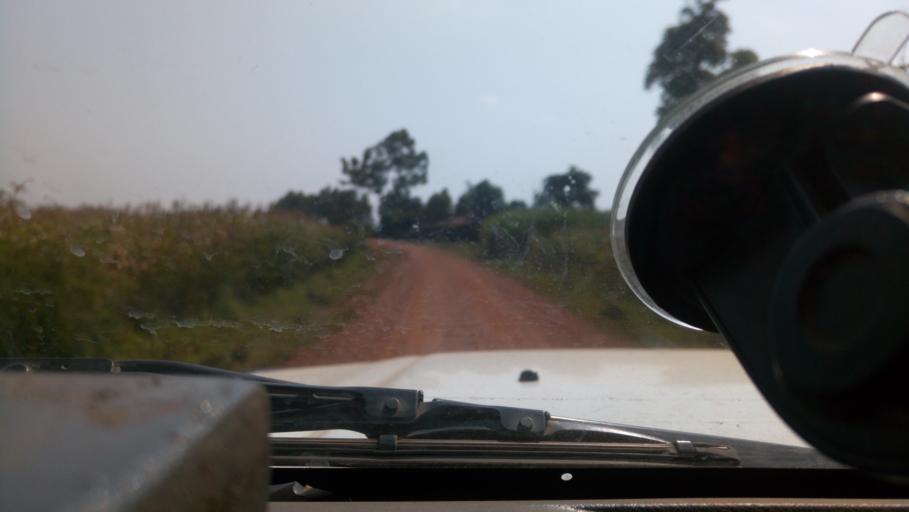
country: KE
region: Kisii
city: Ogembo
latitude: -0.8579
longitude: 34.6128
